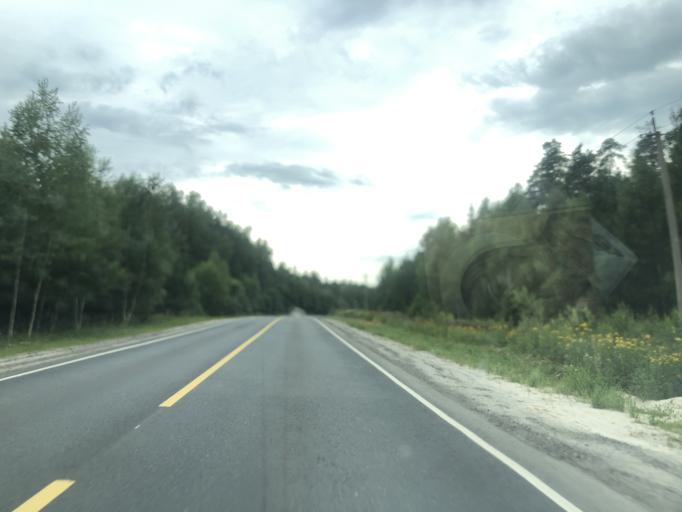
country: RU
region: Ivanovo
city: Pestyaki
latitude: 56.7011
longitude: 42.7292
